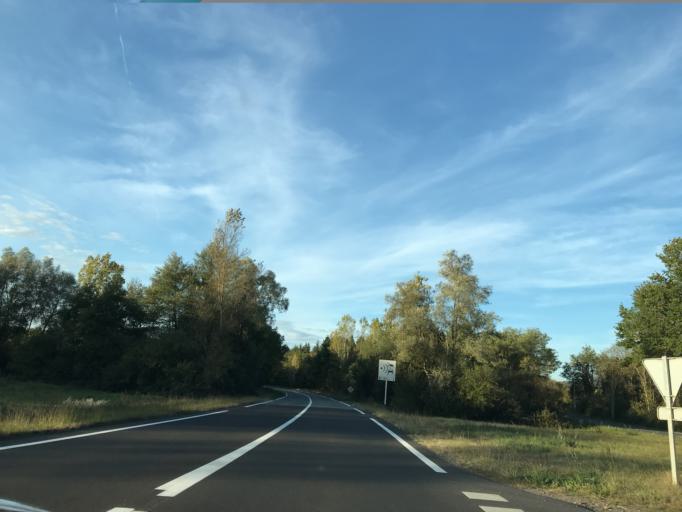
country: FR
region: Auvergne
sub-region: Departement du Puy-de-Dome
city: Puy-Guillaume
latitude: 46.0083
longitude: 3.4872
